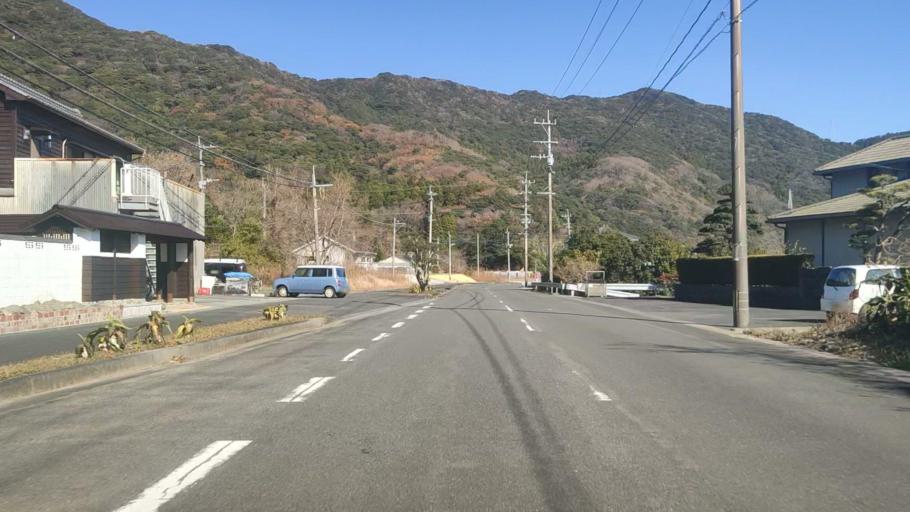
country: JP
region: Oita
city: Saiki
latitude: 32.8043
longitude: 131.9446
